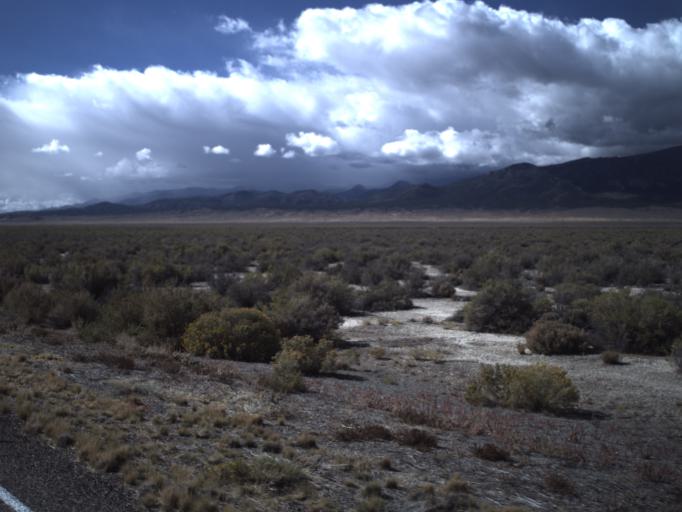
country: US
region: Nevada
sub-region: White Pine County
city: McGill
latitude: 39.0292
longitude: -114.0357
